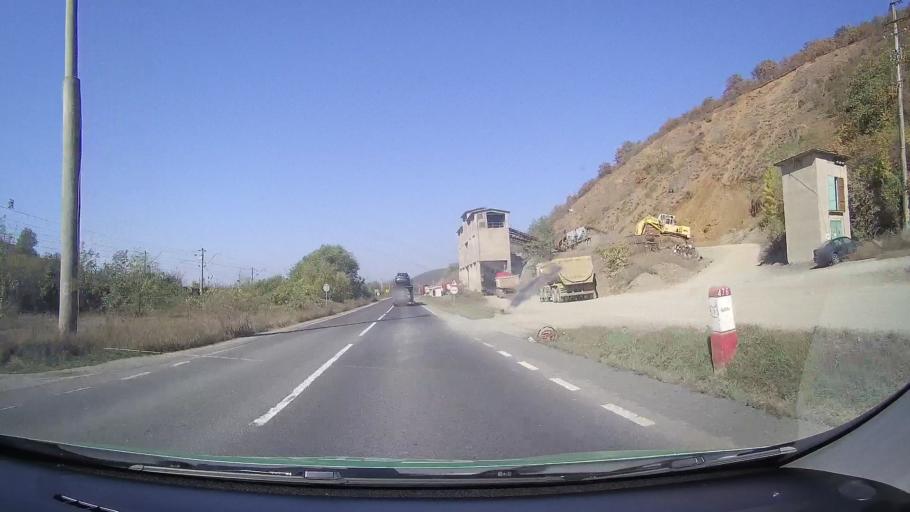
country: RO
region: Arad
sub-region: Comuna Bata
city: Bata
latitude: 46.0577
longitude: 22.0450
